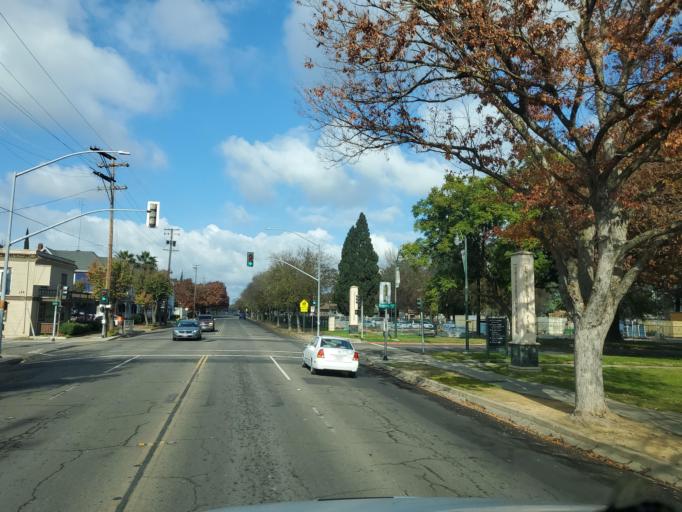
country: US
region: California
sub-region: San Joaquin County
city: Stockton
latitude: 37.9642
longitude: -121.2874
